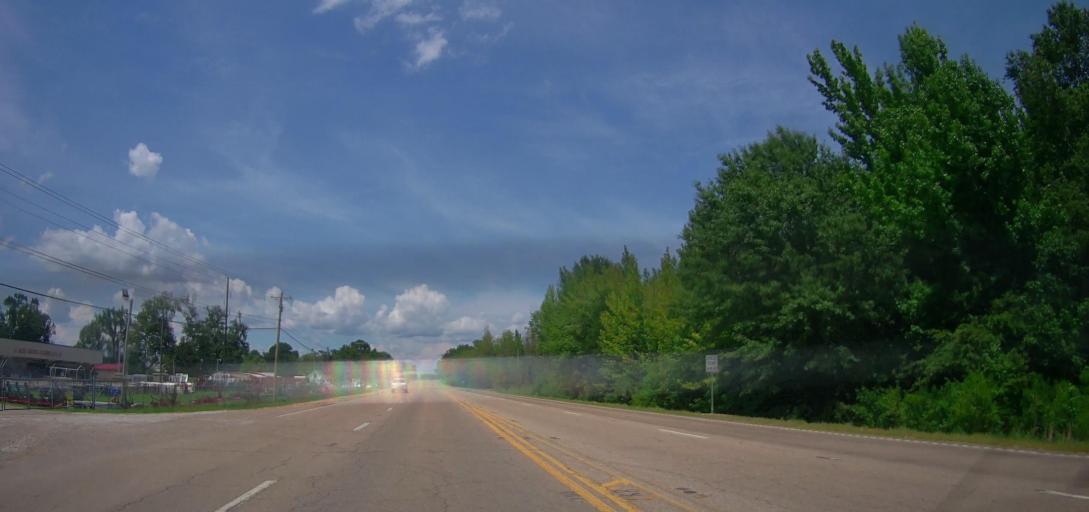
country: US
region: Mississippi
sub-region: Lee County
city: Shannon
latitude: 34.1542
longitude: -88.7194
